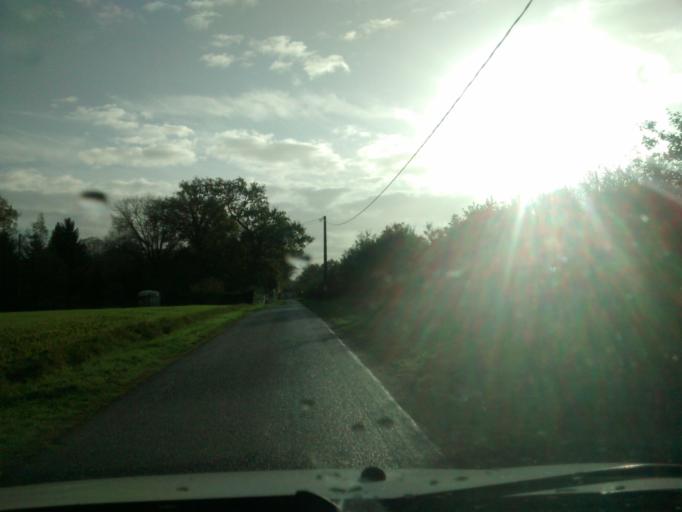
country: FR
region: Brittany
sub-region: Departement d'Ille-et-Vilaine
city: Acigne
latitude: 48.1194
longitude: -1.5606
